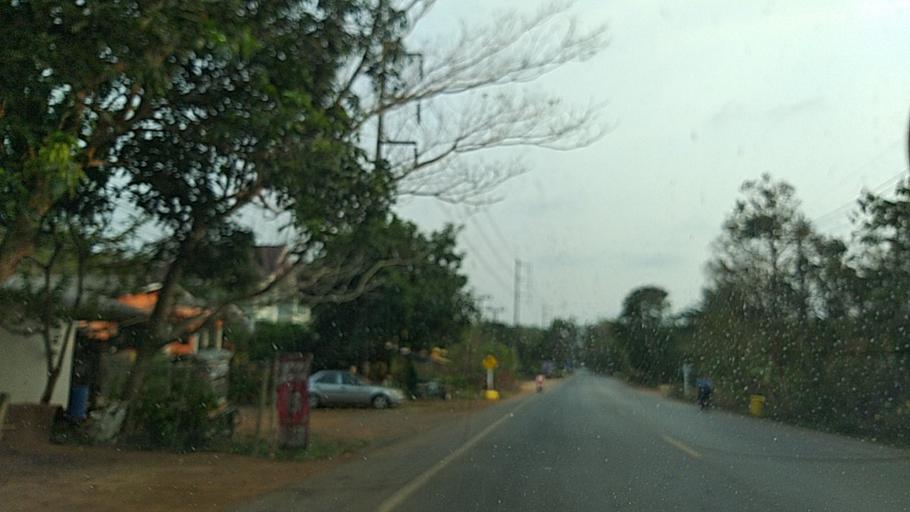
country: TH
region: Trat
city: Laem Ngop
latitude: 12.2227
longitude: 102.3077
